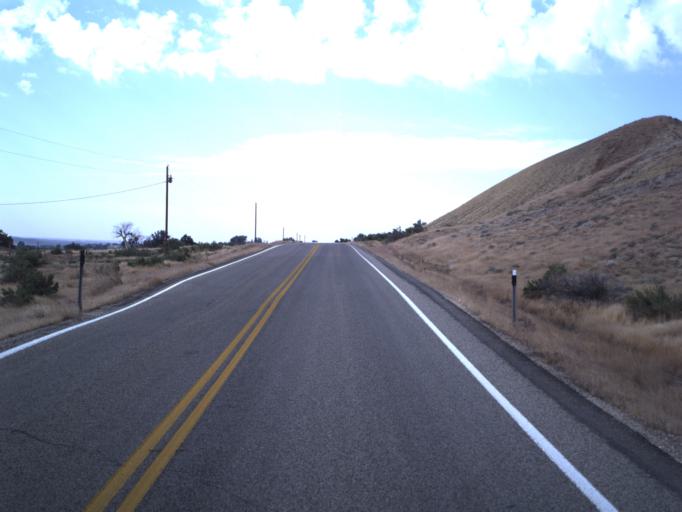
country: US
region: Utah
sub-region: Uintah County
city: Naples
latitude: 40.4280
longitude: -109.3335
